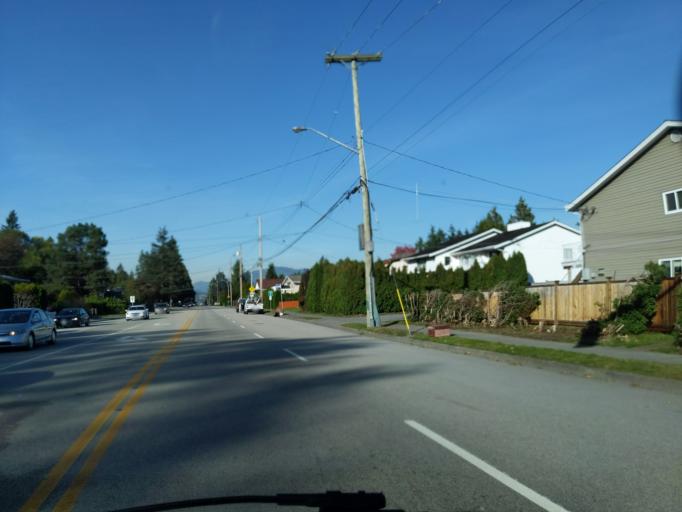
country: CA
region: British Columbia
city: New Westminster
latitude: 49.1918
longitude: -122.8677
